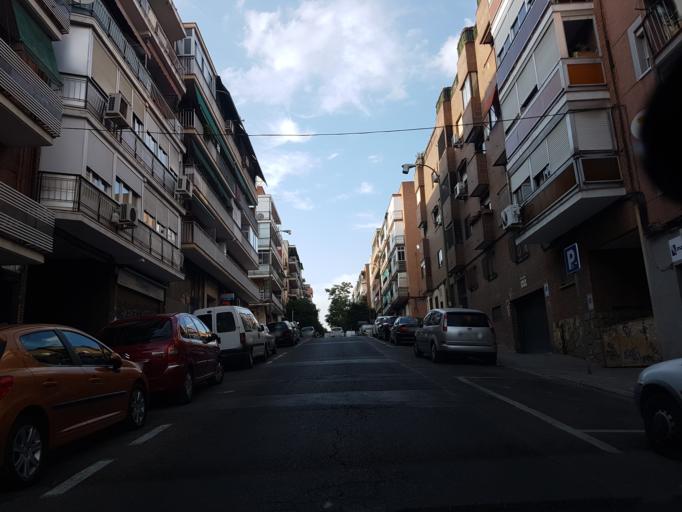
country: ES
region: Madrid
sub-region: Provincia de Madrid
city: Moratalaz
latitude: 40.4297
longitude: -3.6487
